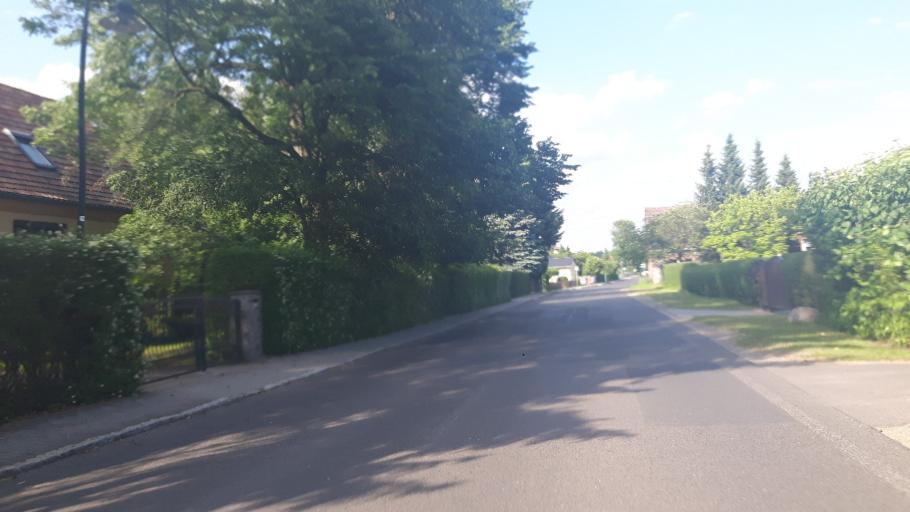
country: DE
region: Brandenburg
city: Melchow
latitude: 52.7442
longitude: 13.7263
